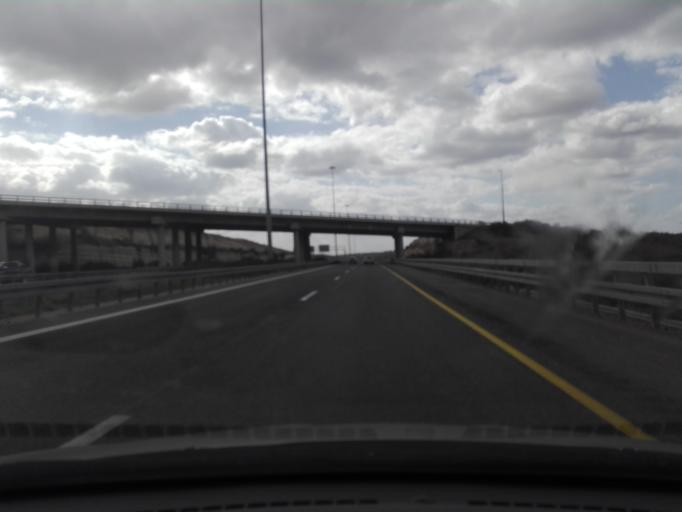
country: IL
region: Haifa
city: Daliyat el Karmil
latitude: 32.6112
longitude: 35.0484
